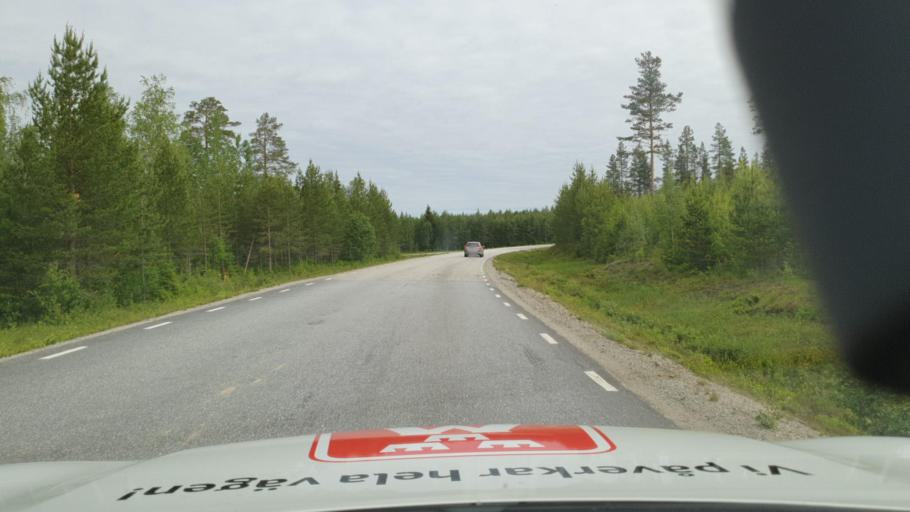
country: SE
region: Vaesterbotten
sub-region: Vindelns Kommun
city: Vindeln
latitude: 64.2196
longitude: 19.7641
